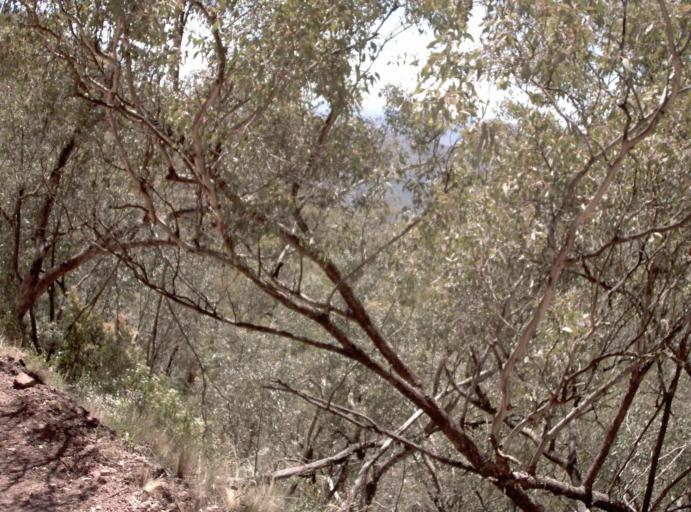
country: AU
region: New South Wales
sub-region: Snowy River
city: Jindabyne
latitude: -36.9960
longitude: 148.3012
